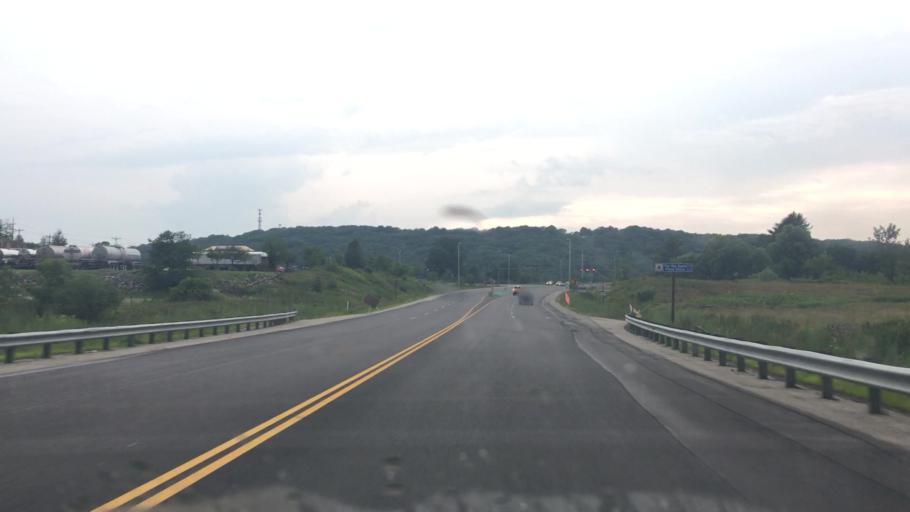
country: US
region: Maine
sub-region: Kennebec County
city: Augusta
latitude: 44.3306
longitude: -69.7560
